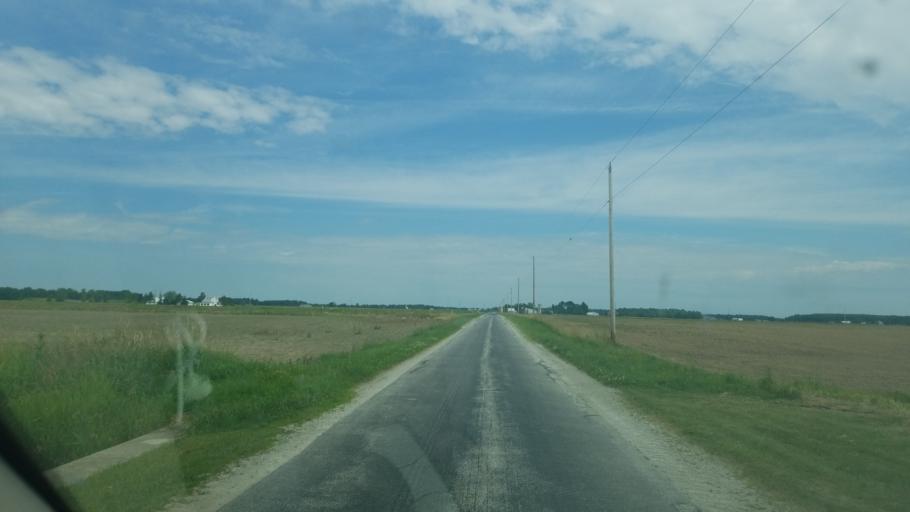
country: US
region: Ohio
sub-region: Wood County
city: North Baltimore
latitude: 41.2276
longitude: -83.5732
